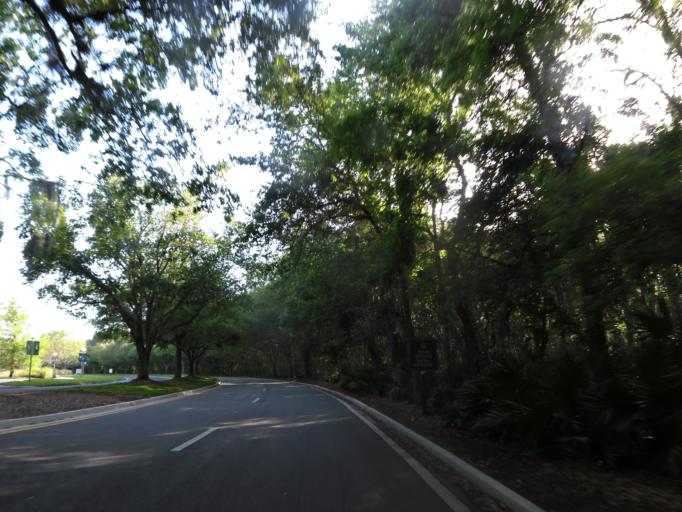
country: US
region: Florida
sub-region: Saint Johns County
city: Villano Beach
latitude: 29.9940
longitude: -81.4758
